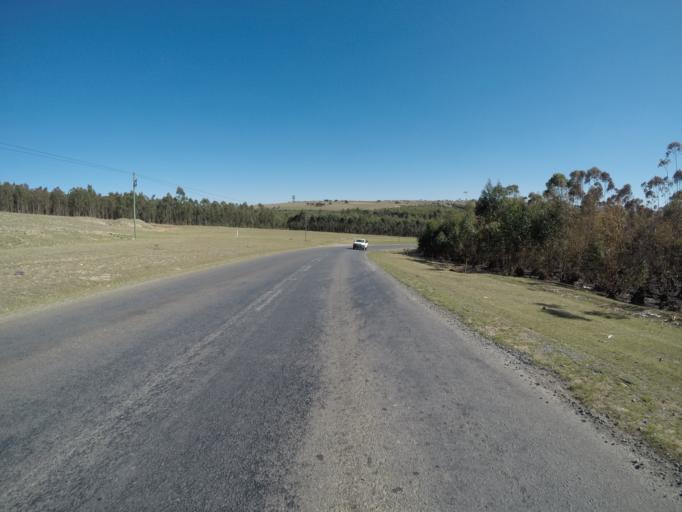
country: ZA
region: Eastern Cape
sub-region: OR Tambo District Municipality
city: Mthatha
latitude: -31.7785
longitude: 28.7375
